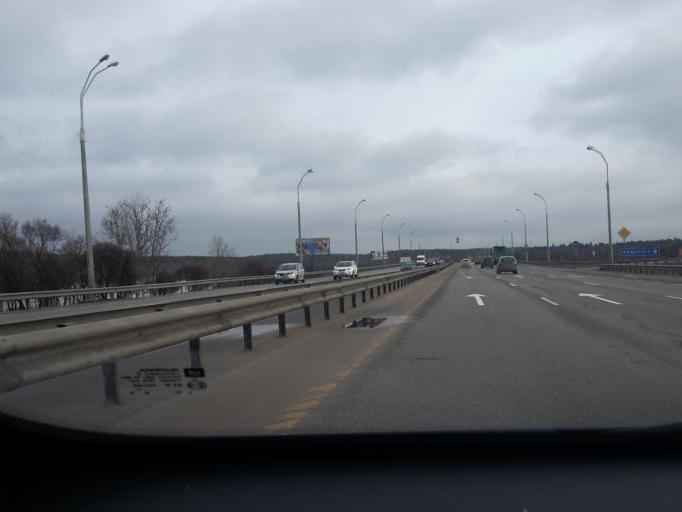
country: BY
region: Minsk
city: Zhdanovichy
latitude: 53.9549
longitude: 27.4508
